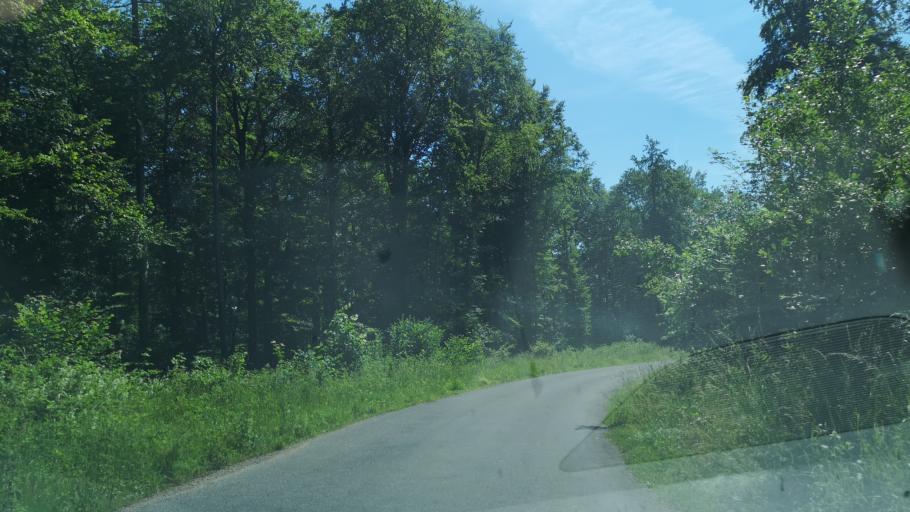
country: FR
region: Lorraine
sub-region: Departement de la Meuse
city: Vigneulles-les-Hattonchatel
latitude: 49.0317
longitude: 5.6425
